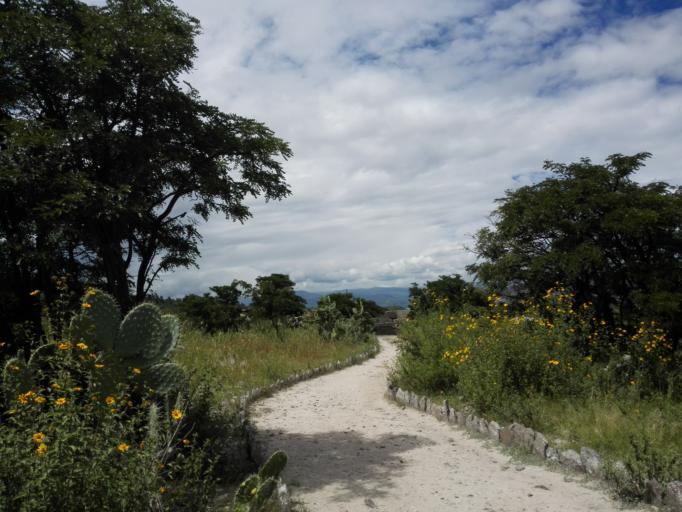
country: PE
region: Ayacucho
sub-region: Provincia de Huamanga
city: Pacaycasa
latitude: -13.0607
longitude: -74.1981
